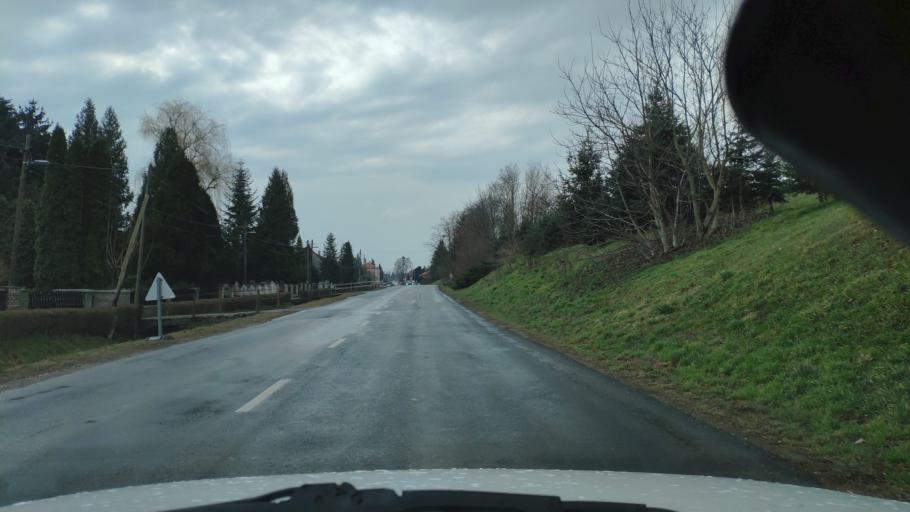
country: HU
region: Zala
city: Nagykanizsa
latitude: 46.4146
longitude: 16.9847
